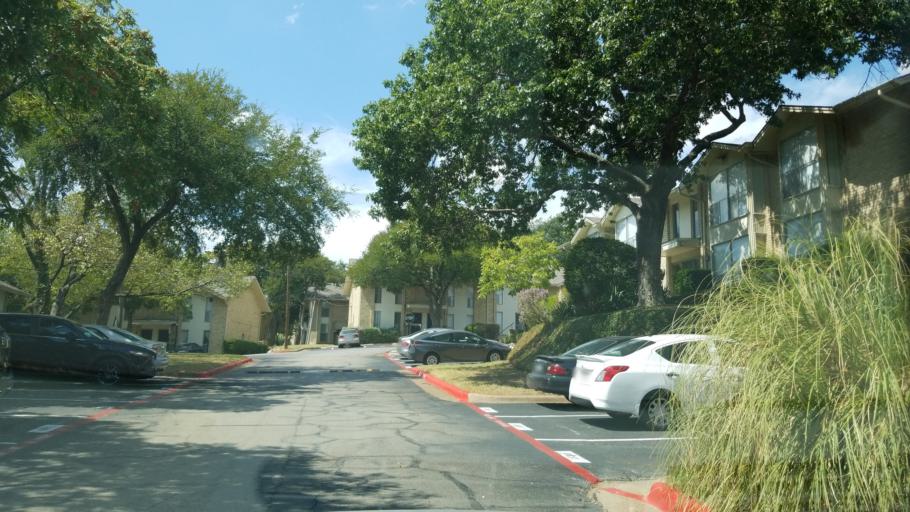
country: US
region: Texas
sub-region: Dallas County
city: Dallas
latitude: 32.7634
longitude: -96.8489
